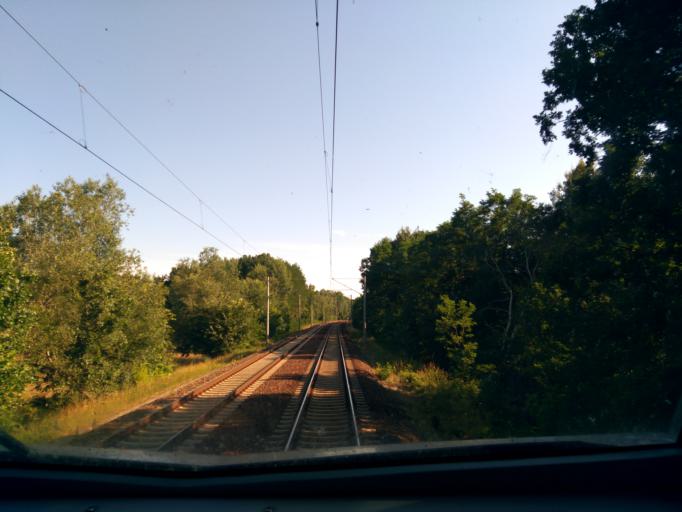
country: DE
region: Brandenburg
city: Halbe
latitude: 52.0506
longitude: 13.7206
